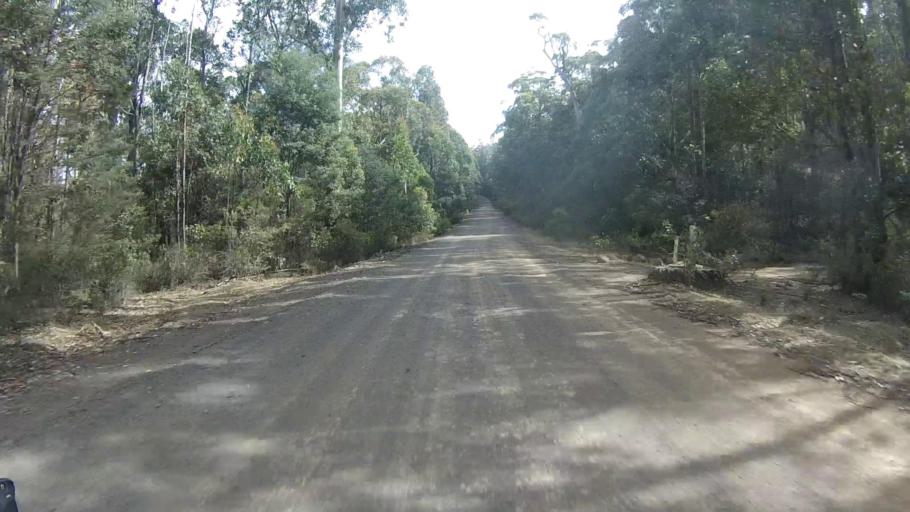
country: AU
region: Tasmania
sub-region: Sorell
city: Sorell
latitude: -42.7503
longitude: 147.8284
